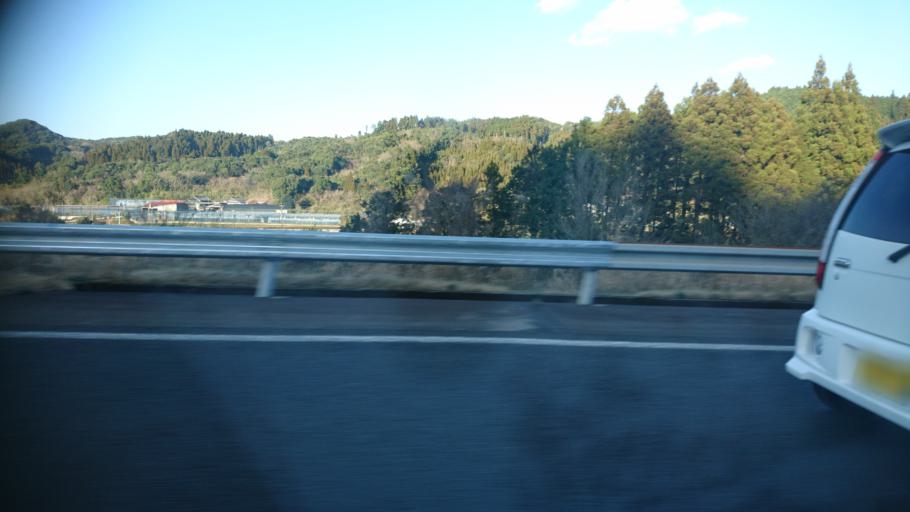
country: JP
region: Miyazaki
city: Miyakonojo
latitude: 31.7935
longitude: 131.1770
